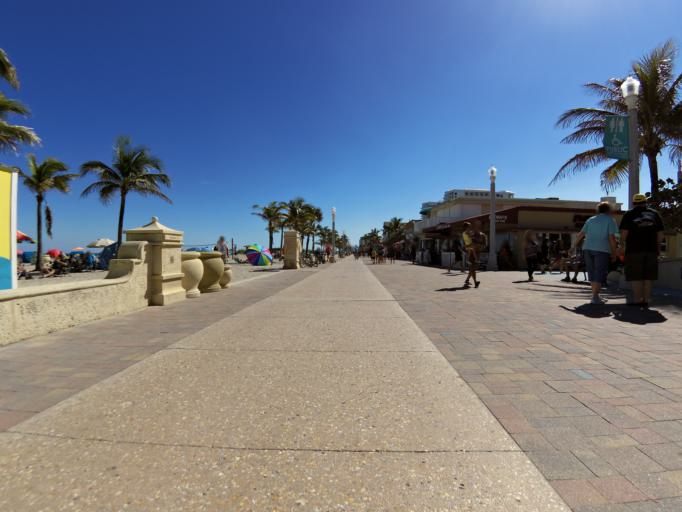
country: US
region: Florida
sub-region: Broward County
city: Hollywood
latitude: 26.0220
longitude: -80.1151
